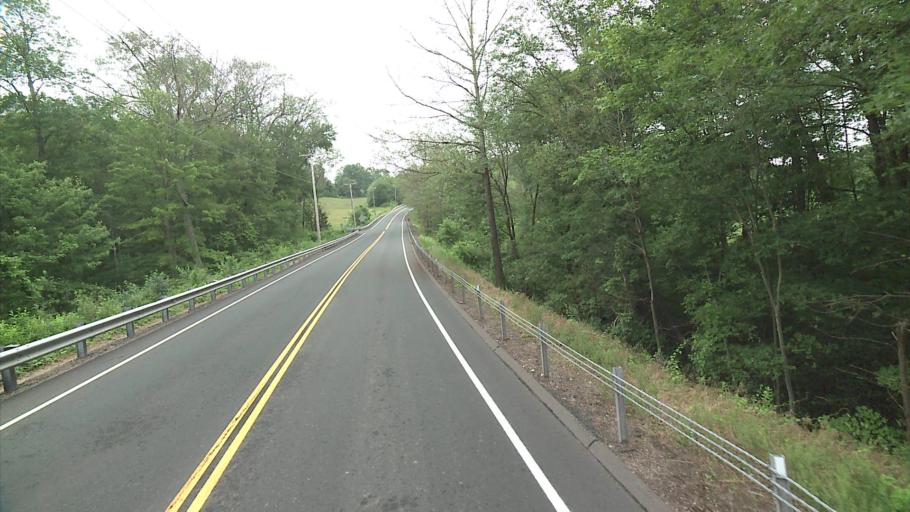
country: US
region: Connecticut
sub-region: Hartford County
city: Terramuggus
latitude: 41.6968
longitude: -72.4559
